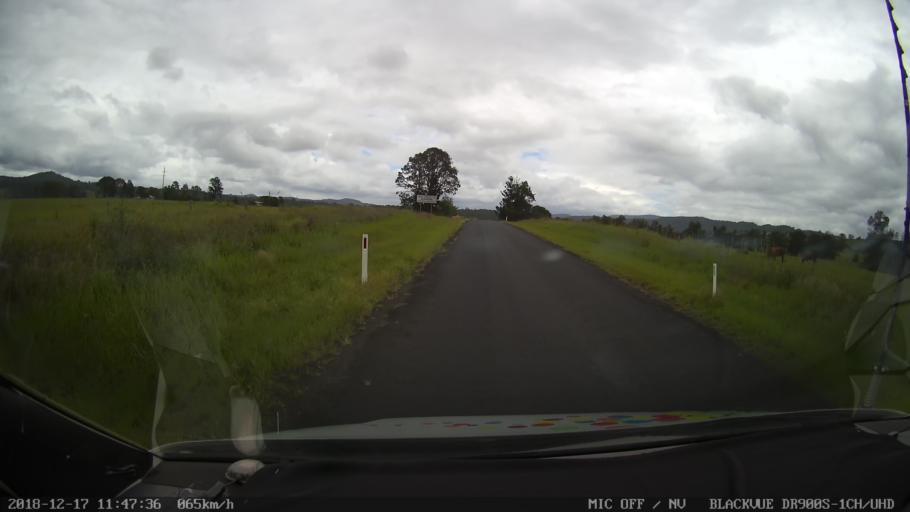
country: AU
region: New South Wales
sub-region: Kyogle
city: Kyogle
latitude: -28.6256
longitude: 152.5912
